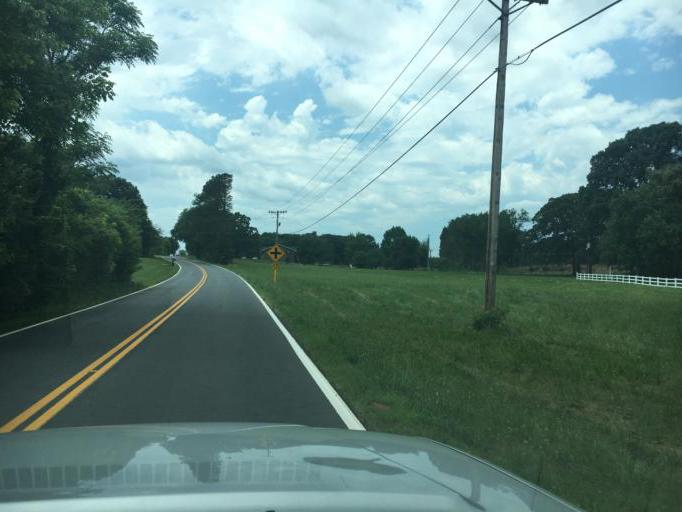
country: US
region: South Carolina
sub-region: Spartanburg County
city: Duncan
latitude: 34.8758
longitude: -82.1753
